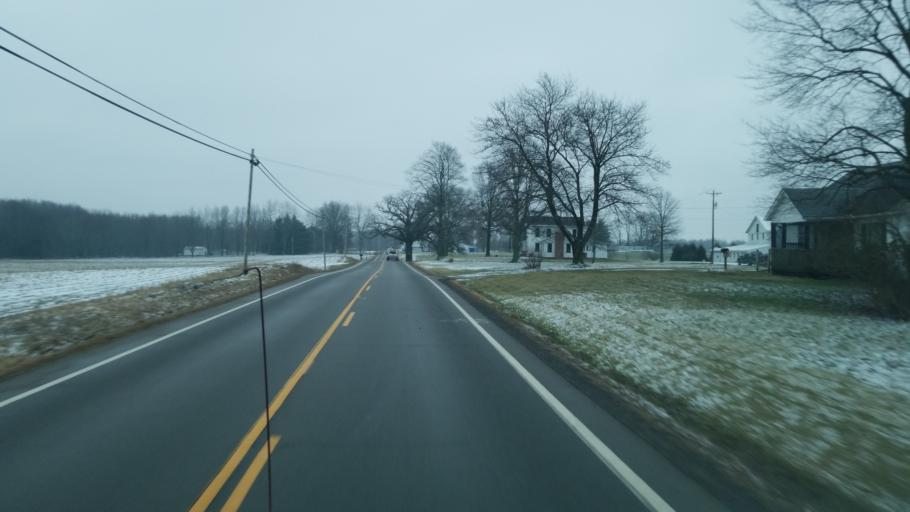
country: US
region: Ohio
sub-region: Wayne County
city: Shreve
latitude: 40.7666
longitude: -82.0419
